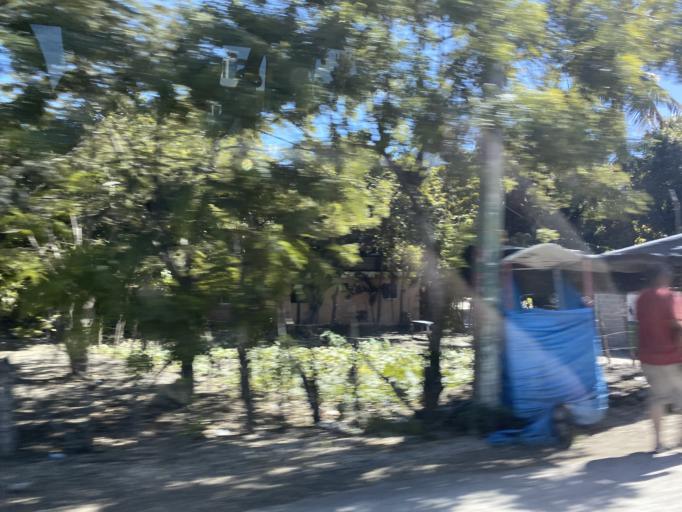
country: DO
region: Puerto Plata
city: Imbert
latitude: 19.8238
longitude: -70.7756
